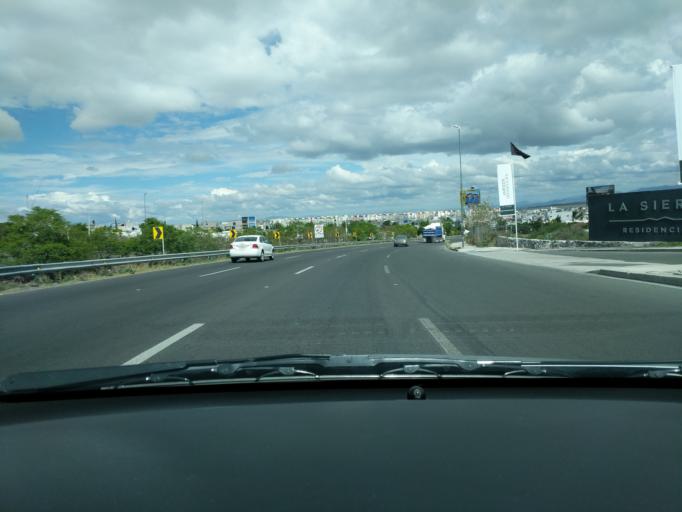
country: MX
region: Queretaro
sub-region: El Marques
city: La Pradera
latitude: 20.6605
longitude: -100.3446
